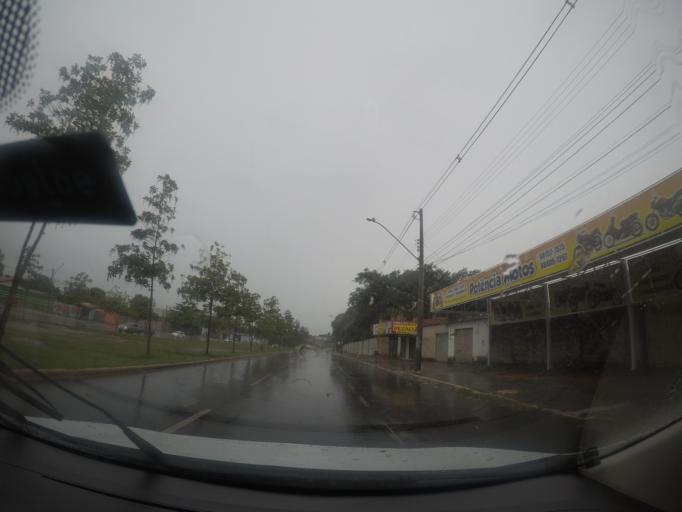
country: BR
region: Goias
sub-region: Goiania
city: Goiania
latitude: -16.6162
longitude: -49.3405
